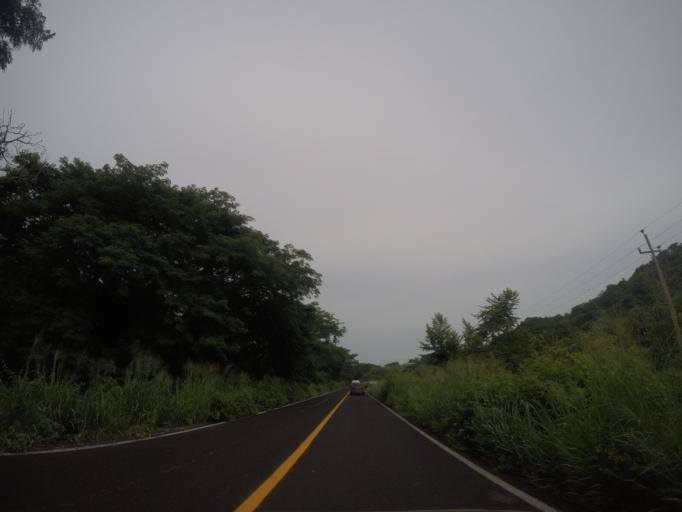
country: MX
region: Oaxaca
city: San Pedro Mixtepec
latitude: 15.9507
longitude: -97.2709
